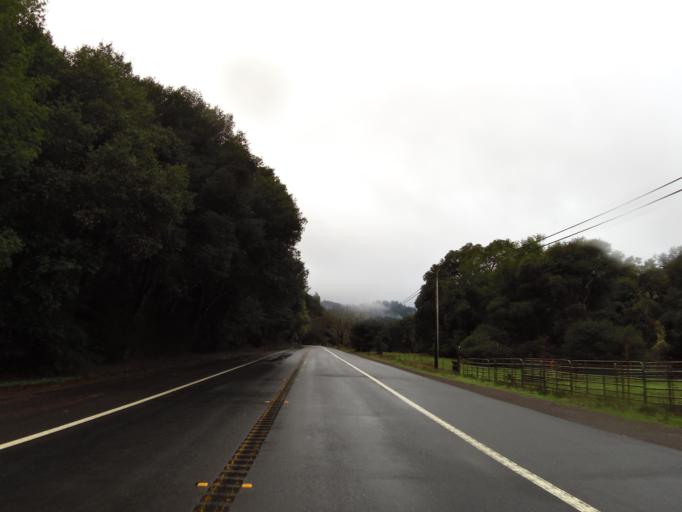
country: US
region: California
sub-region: Mendocino County
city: Boonville
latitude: 38.9151
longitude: -123.2505
